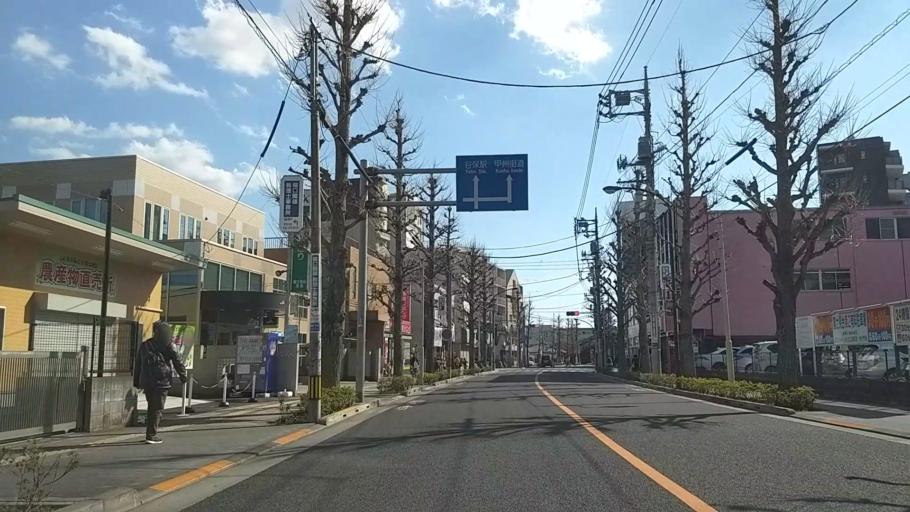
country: JP
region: Tokyo
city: Kokubunji
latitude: 35.6834
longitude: 139.4473
